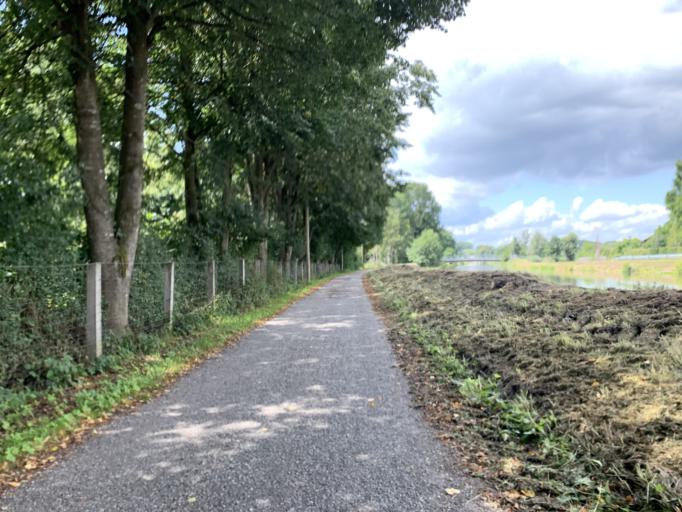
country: DE
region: Bavaria
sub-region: Upper Bavaria
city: Zolling
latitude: 48.4494
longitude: 11.7597
